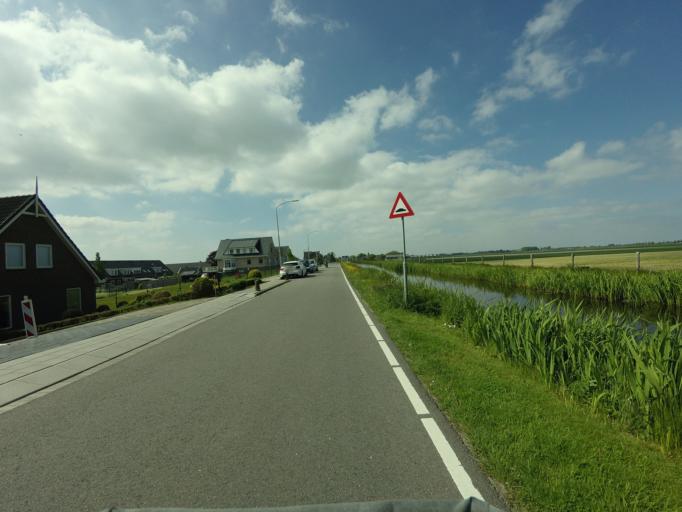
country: NL
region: South Holland
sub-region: Gemeente Nieuwkoop
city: Nieuwkoop
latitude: 52.1851
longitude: 4.7789
